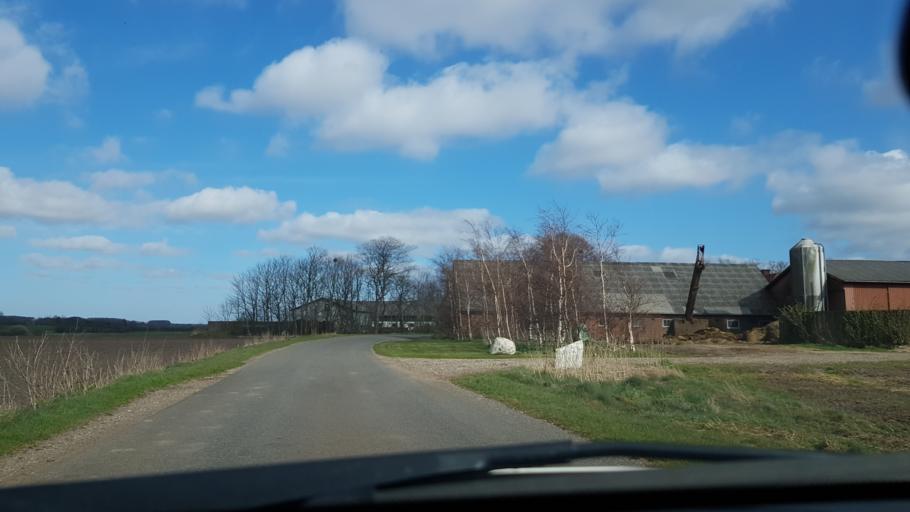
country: DK
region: South Denmark
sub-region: Vejen Kommune
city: Rodding
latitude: 55.3744
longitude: 8.9728
